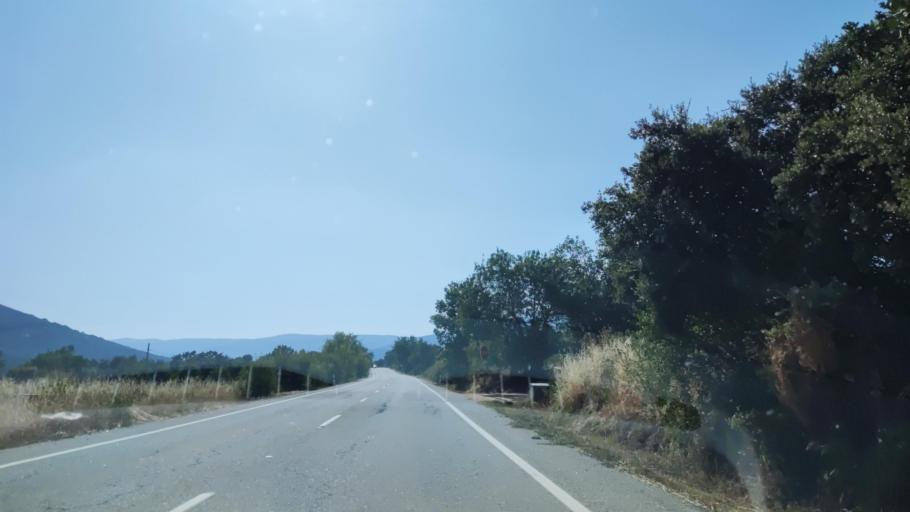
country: ES
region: Madrid
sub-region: Provincia de Madrid
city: Canencia
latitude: 40.9468
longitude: -3.7474
